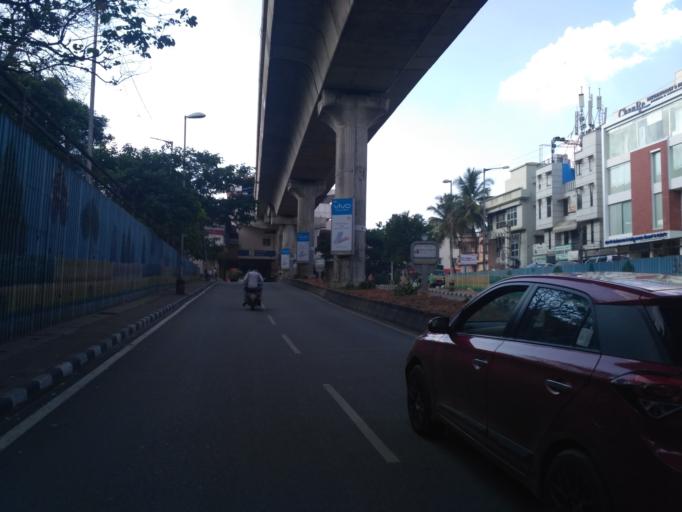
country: IN
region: Karnataka
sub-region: Bangalore Urban
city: Bangalore
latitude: 12.9987
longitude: 77.5500
